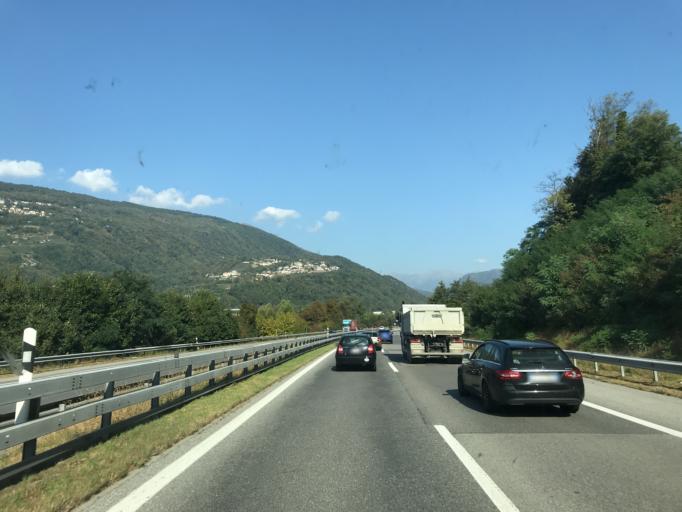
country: CH
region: Ticino
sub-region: Lugano District
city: Bioggio
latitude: 46.0049
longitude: 8.9148
